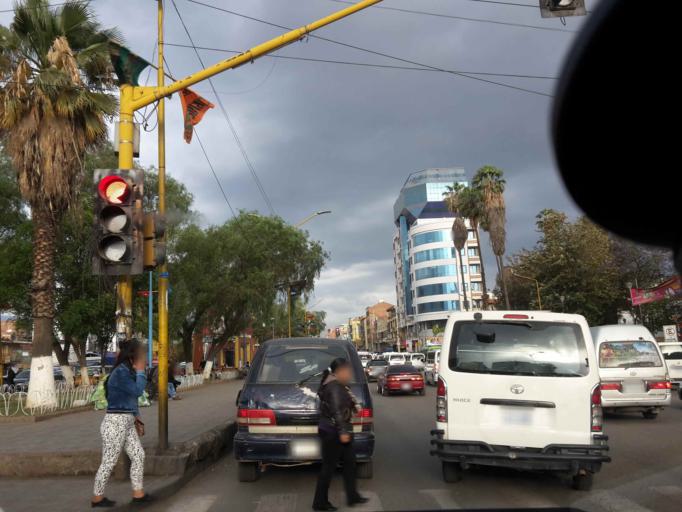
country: BO
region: Cochabamba
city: Sipe Sipe
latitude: -17.3943
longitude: -66.2816
